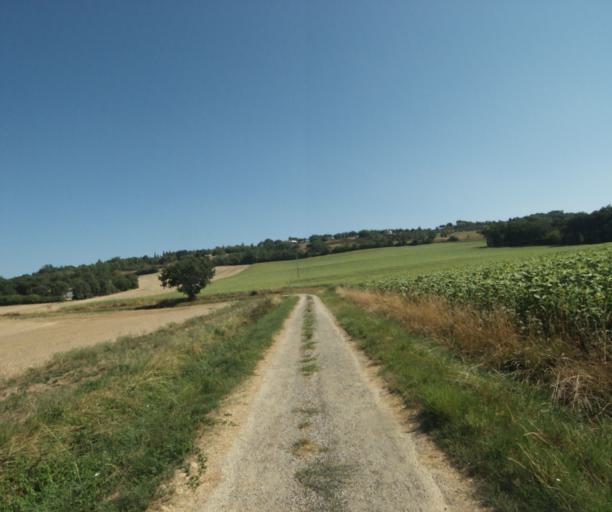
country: FR
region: Midi-Pyrenees
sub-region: Departement de la Haute-Garonne
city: Saint-Felix-Lauragais
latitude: 43.5111
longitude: 1.9188
